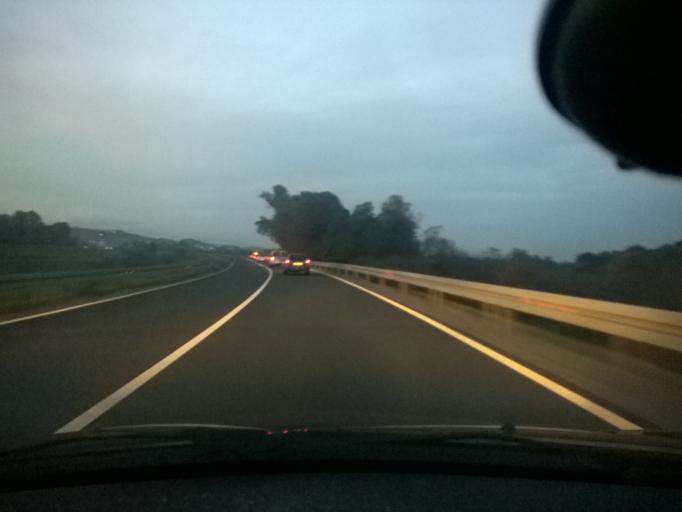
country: HR
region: Zagrebacka
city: Pojatno
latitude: 45.8896
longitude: 15.8223
